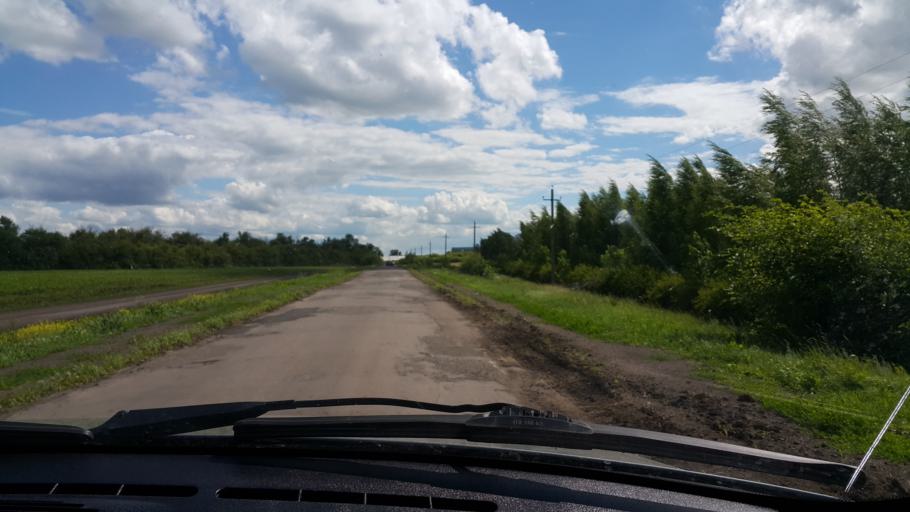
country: RU
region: Tambov
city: Satinka
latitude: 52.3897
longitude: 41.6637
